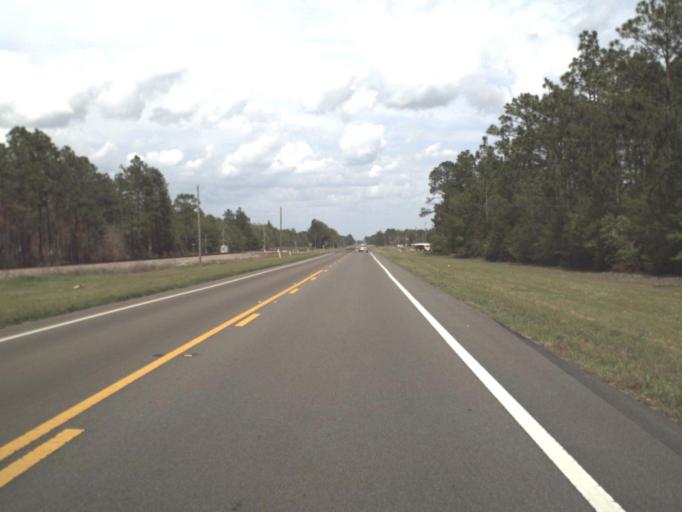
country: US
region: Florida
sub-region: Santa Rosa County
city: East Milton
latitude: 30.6918
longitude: -86.8113
